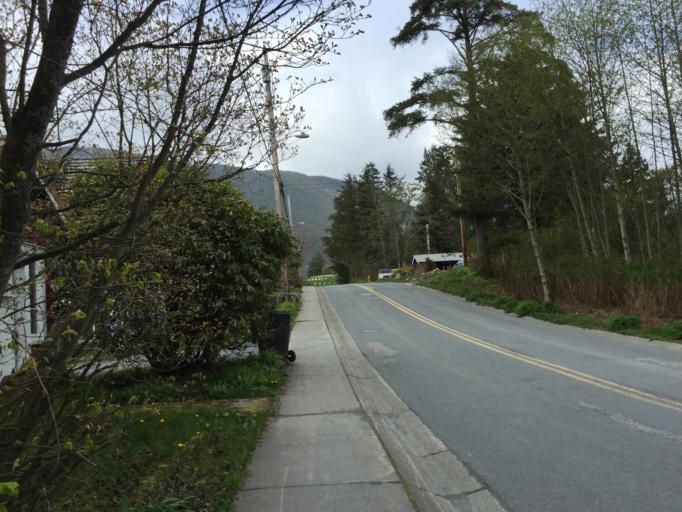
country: US
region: Alaska
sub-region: Sitka City and Borough
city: Sitka
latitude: 57.0521
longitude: -135.3248
